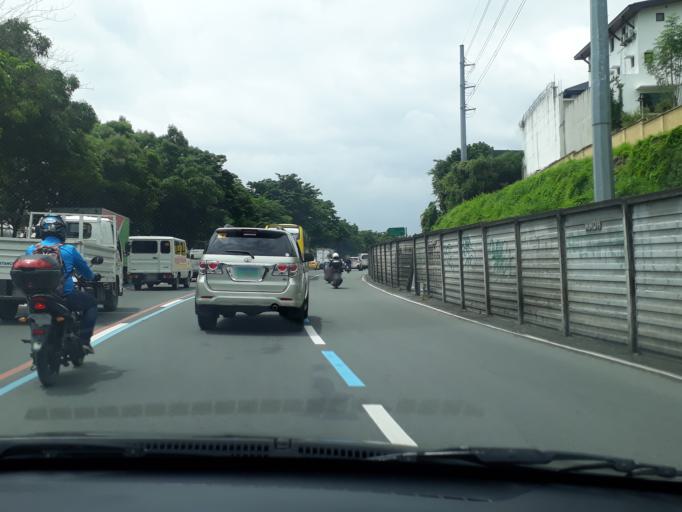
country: PH
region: Calabarzon
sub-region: Province of Rizal
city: Pateros
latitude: 14.5391
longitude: 121.0571
